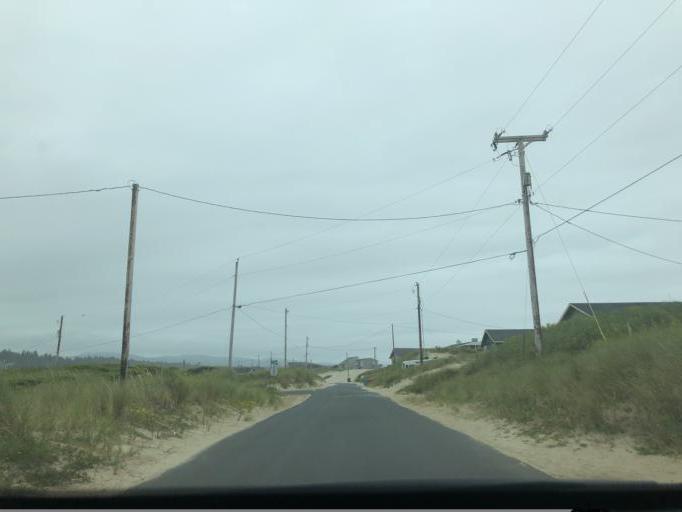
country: US
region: Oregon
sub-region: Lincoln County
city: Waldport
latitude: 44.4307
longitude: -124.0827
